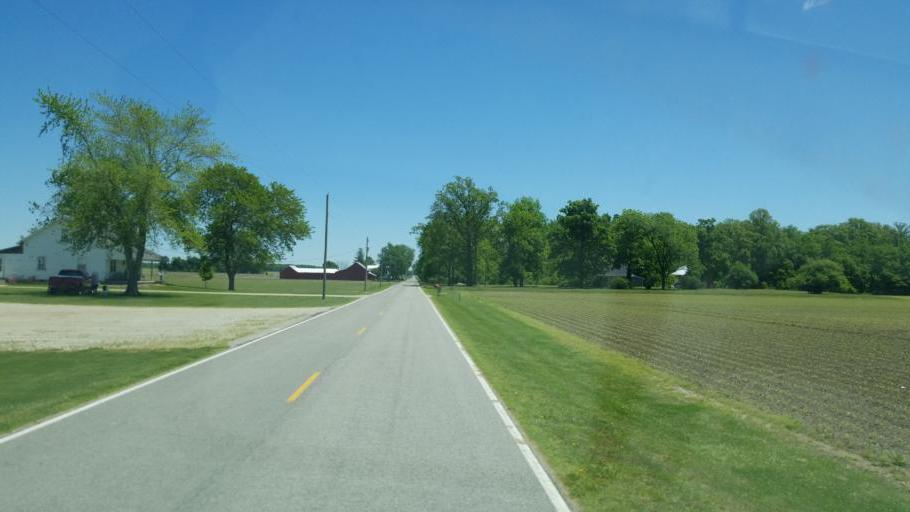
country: US
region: Indiana
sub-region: Randolph County
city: Union City
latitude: 40.2815
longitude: -84.7611
